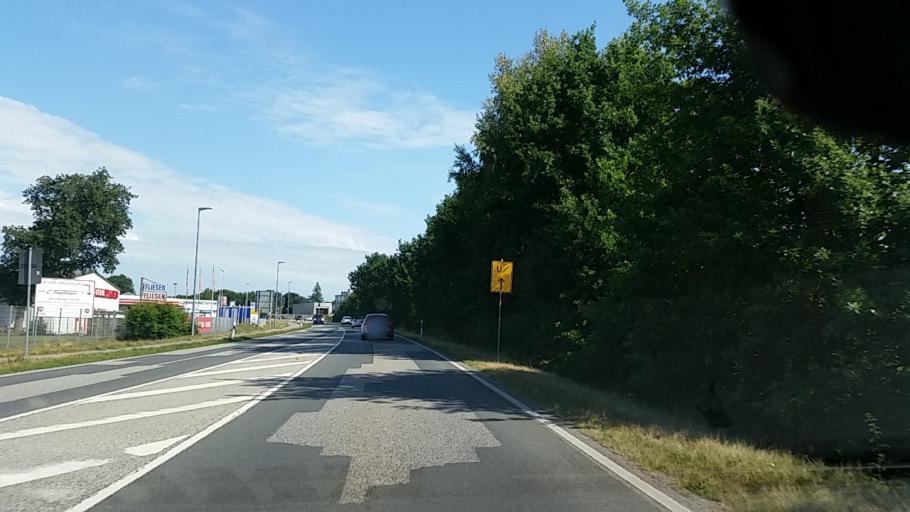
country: DE
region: Schleswig-Holstein
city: Oersdorf
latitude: 53.8283
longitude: 9.9732
